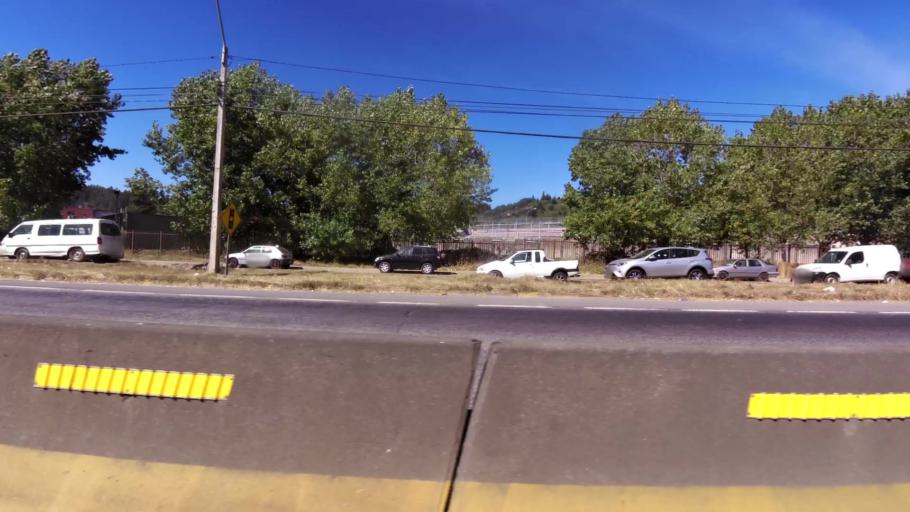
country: CL
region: Biobio
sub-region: Provincia de Concepcion
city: Concepcion
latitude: -36.8057
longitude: -73.0242
